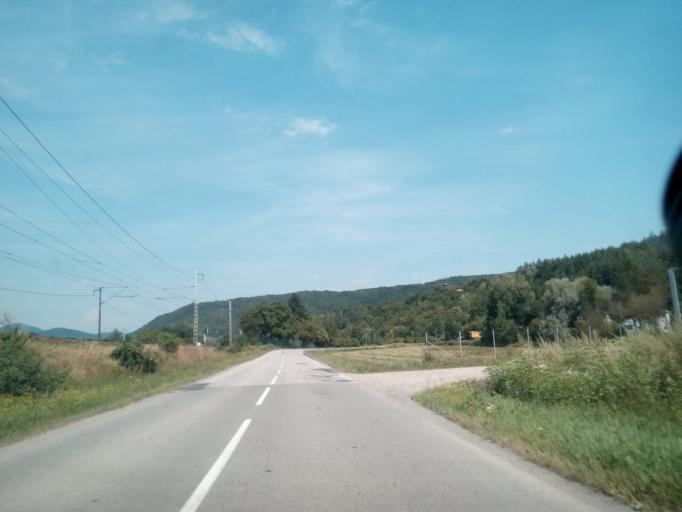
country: SK
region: Kosicky
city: Kosice
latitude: 48.8089
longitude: 21.2349
